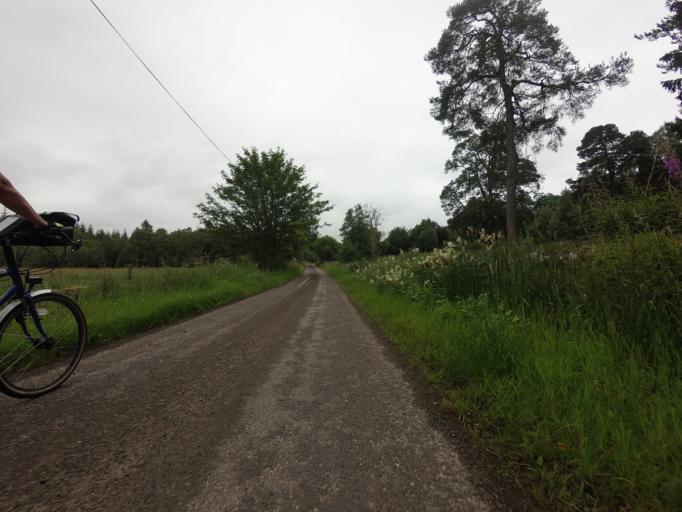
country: GB
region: Scotland
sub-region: Highland
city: Evanton
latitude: 57.9822
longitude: -4.4178
